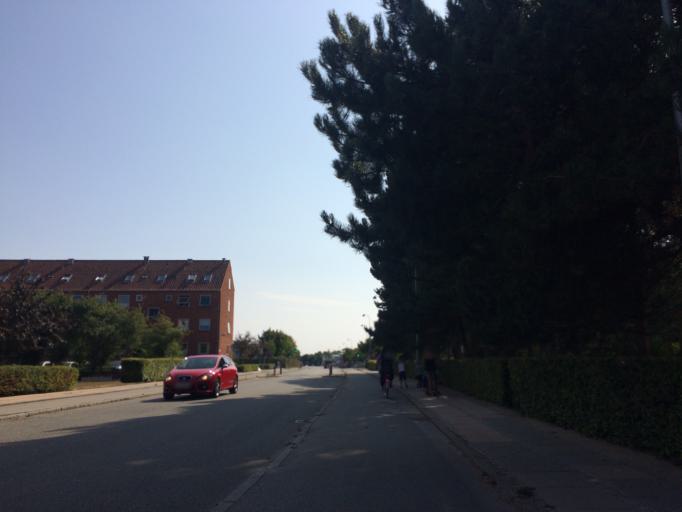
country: DK
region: Capital Region
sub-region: Hvidovre Kommune
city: Hvidovre
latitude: 55.6451
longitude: 12.4723
